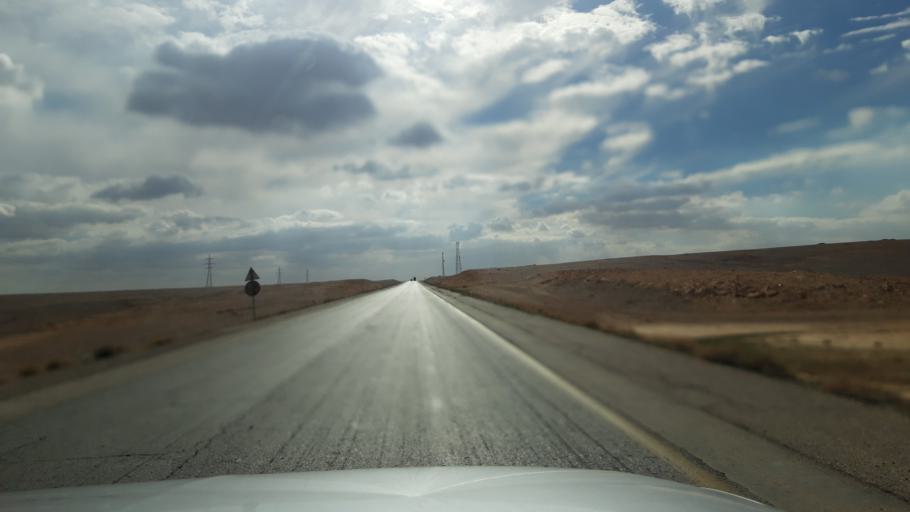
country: JO
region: Amman
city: Al Azraq ash Shamali
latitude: 31.7413
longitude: 36.5305
